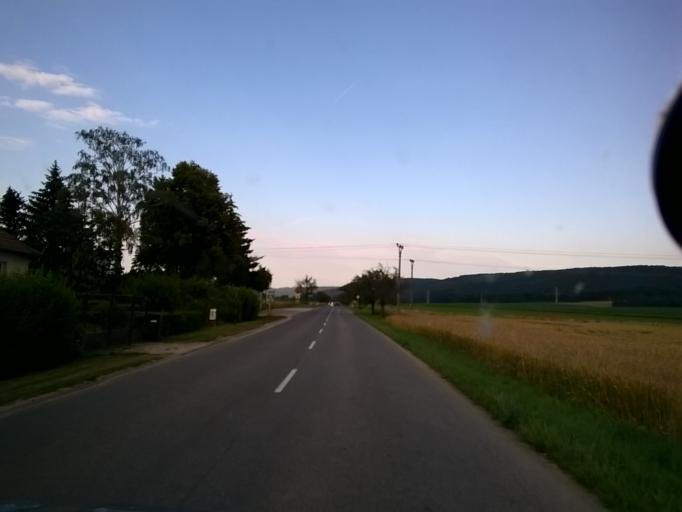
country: SK
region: Trnavsky
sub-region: Okres Senica
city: Senica
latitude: 48.6134
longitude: 17.4273
